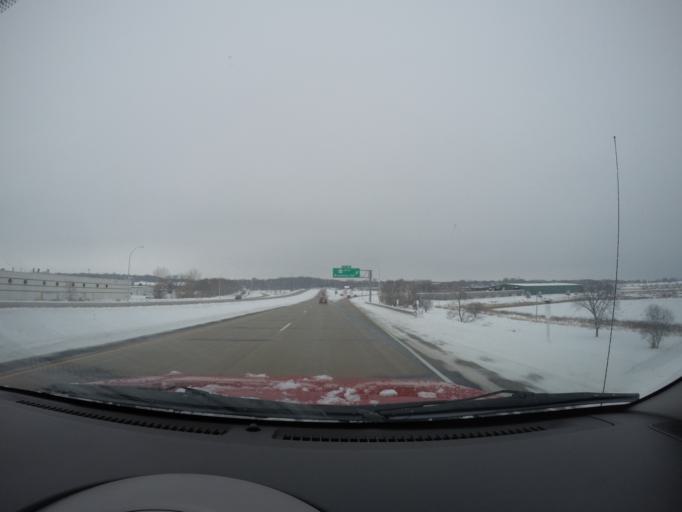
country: US
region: Minnesota
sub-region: Olmsted County
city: Rochester
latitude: 43.9753
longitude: -92.4559
